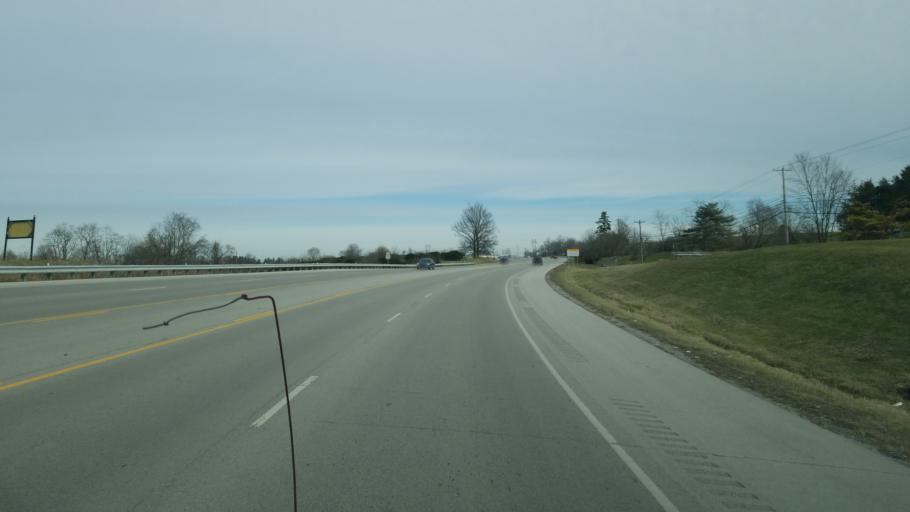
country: US
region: Ohio
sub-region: Brown County
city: Aberdeen
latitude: 38.6224
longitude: -83.8076
